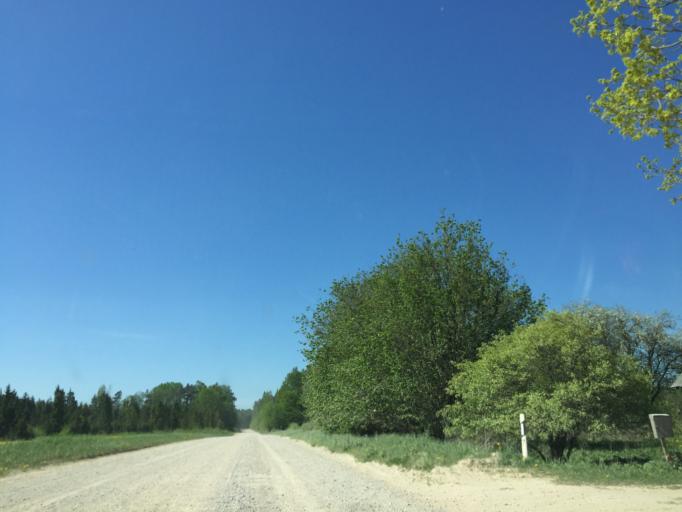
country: LV
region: Kegums
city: Kegums
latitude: 56.8926
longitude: 24.8066
